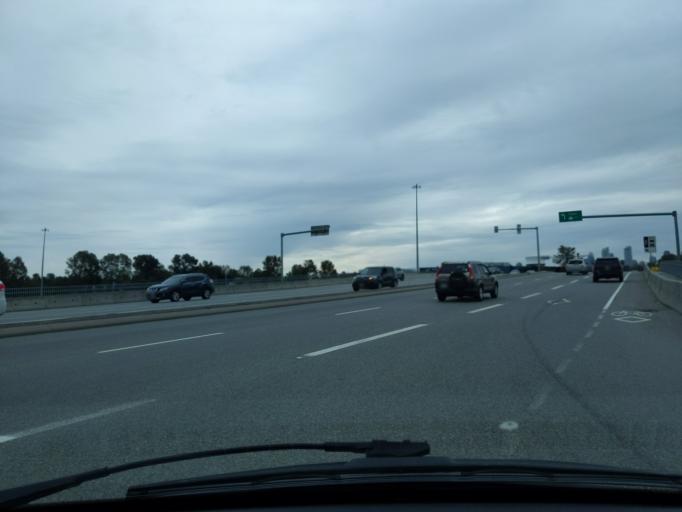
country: CA
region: British Columbia
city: Burnaby
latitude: 49.2588
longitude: -123.0041
